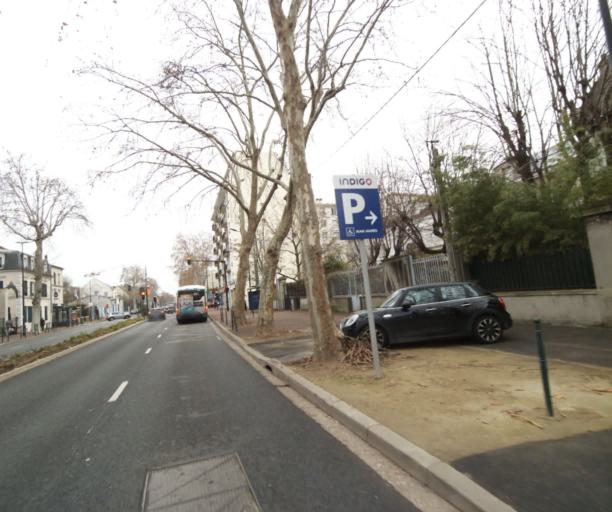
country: FR
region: Ile-de-France
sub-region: Departement des Hauts-de-Seine
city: Rueil-Malmaison
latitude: 48.8783
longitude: 2.1765
